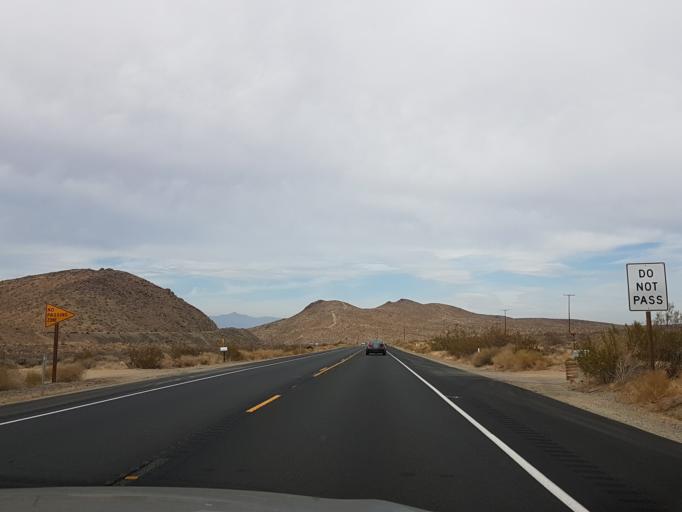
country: US
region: California
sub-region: Kern County
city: Ridgecrest
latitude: 35.5392
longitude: -117.6861
